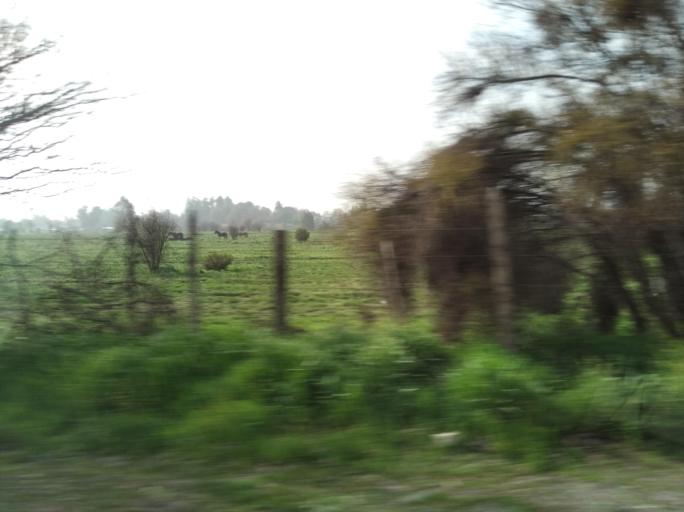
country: CL
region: Santiago Metropolitan
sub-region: Provincia de Chacabuco
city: Lampa
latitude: -33.1707
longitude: -70.8945
